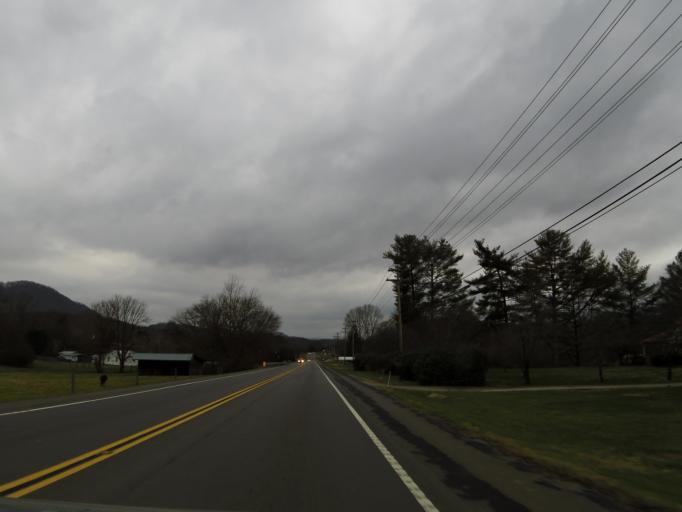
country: US
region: Tennessee
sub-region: Grainger County
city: Rutledge
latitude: 36.2851
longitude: -83.5033
